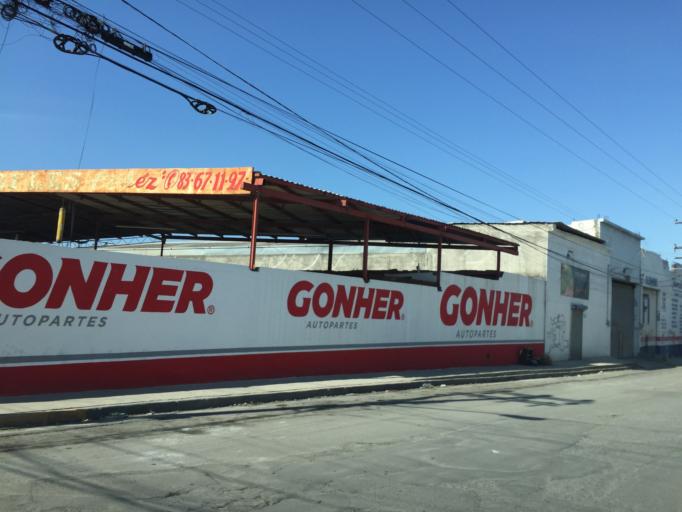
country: MX
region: Nuevo Leon
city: Guadalupe
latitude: 25.6827
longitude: -100.2355
